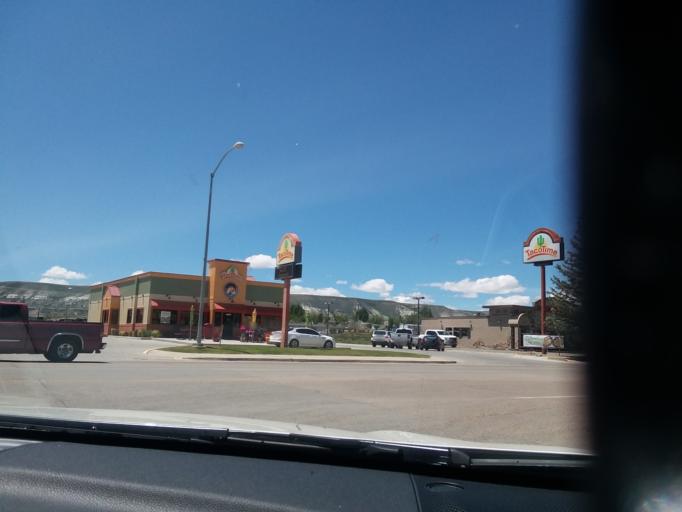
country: US
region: Wyoming
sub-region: Sweetwater County
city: Rock Springs
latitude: 41.6117
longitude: -109.2303
